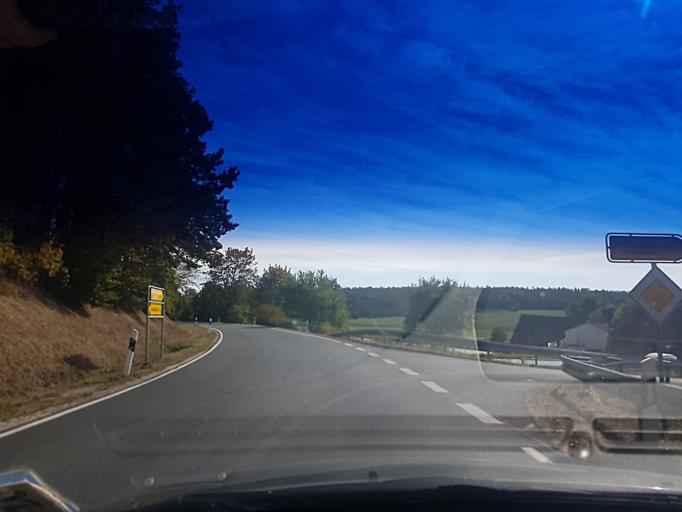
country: DE
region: Bavaria
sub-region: Regierungsbezirk Mittelfranken
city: Wachenroth
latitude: 49.7714
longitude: 10.7205
